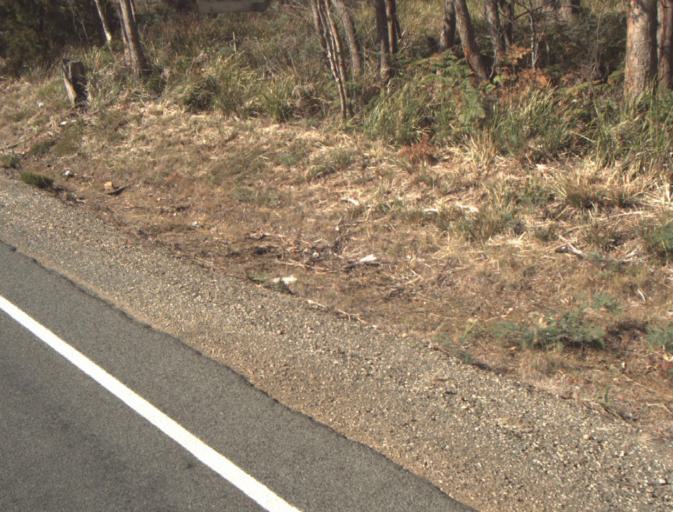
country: AU
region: Tasmania
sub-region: Launceston
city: Mayfield
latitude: -41.3398
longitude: 147.1442
